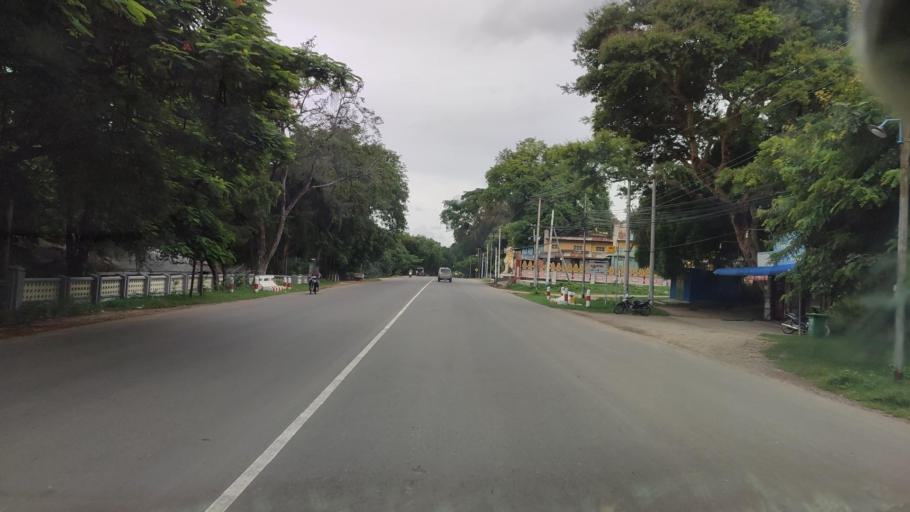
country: MM
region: Mandalay
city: Meiktila
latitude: 20.8709
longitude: 95.8678
